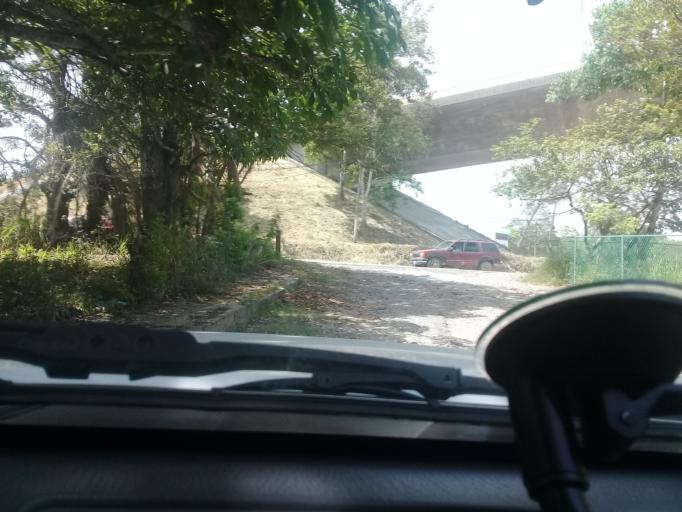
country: MX
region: Veracruz
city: Anahuac
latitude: 22.2258
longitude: -97.8322
